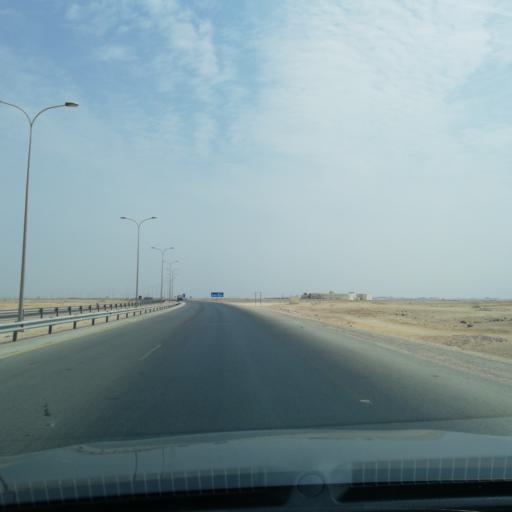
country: OM
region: Zufar
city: Salalah
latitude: 17.6502
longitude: 54.0552
